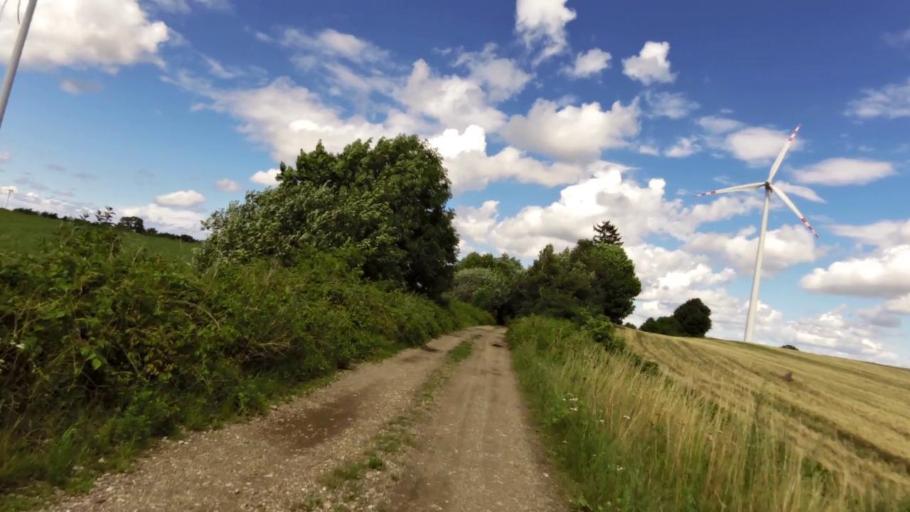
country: PL
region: West Pomeranian Voivodeship
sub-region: Powiat slawienski
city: Slawno
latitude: 54.5148
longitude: 16.7115
